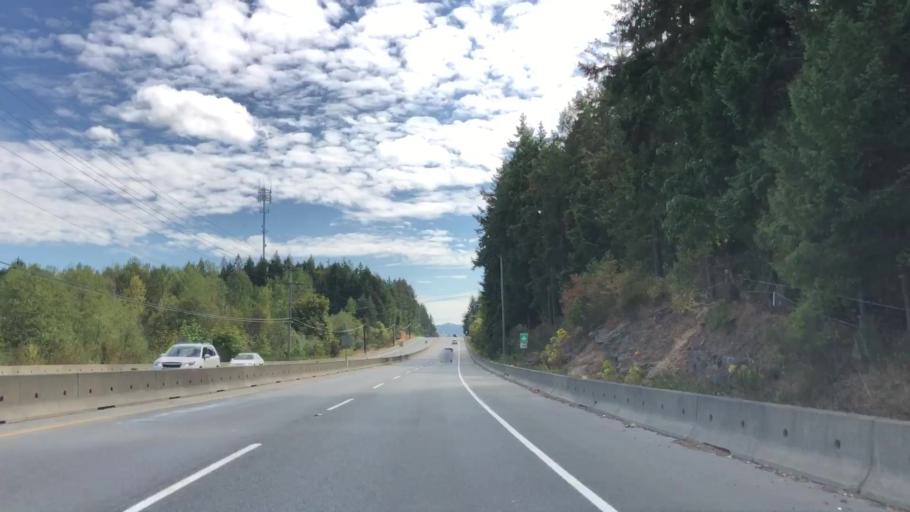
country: CA
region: British Columbia
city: North Cowichan
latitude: 48.9025
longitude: -123.7211
